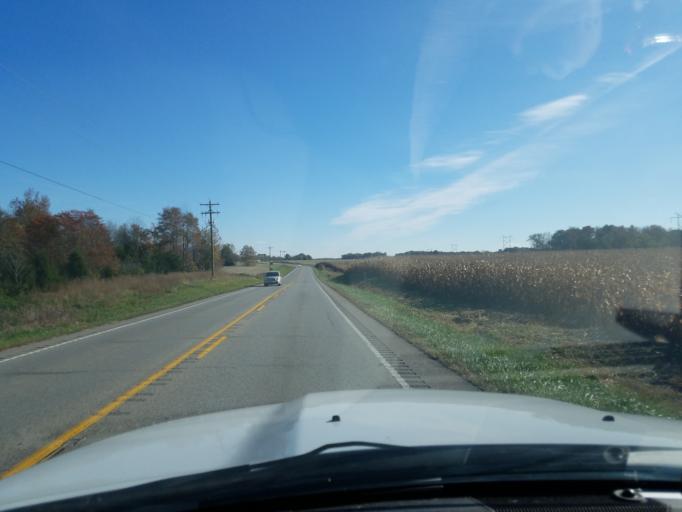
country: US
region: Indiana
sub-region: Jennings County
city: Country Squire Lakes
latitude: 38.9722
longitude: -85.7636
